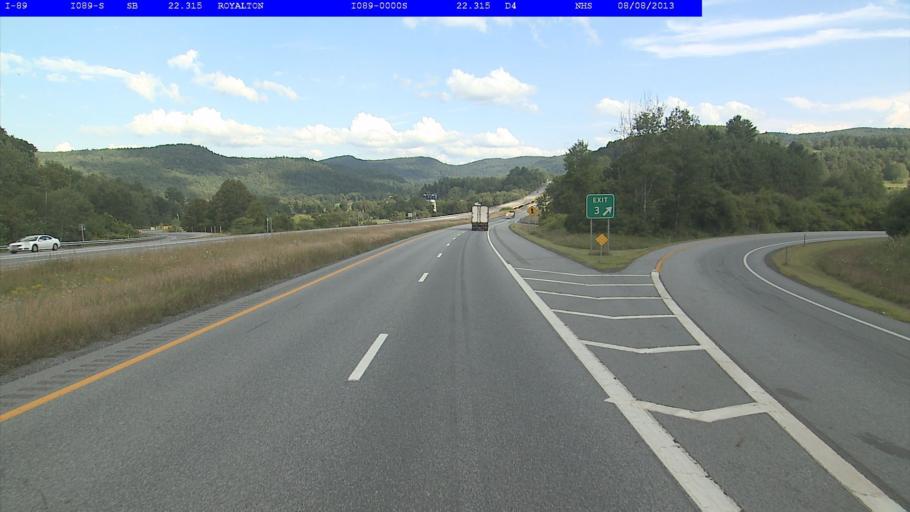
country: US
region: Vermont
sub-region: Orange County
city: Randolph
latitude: 43.8291
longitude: -72.5827
